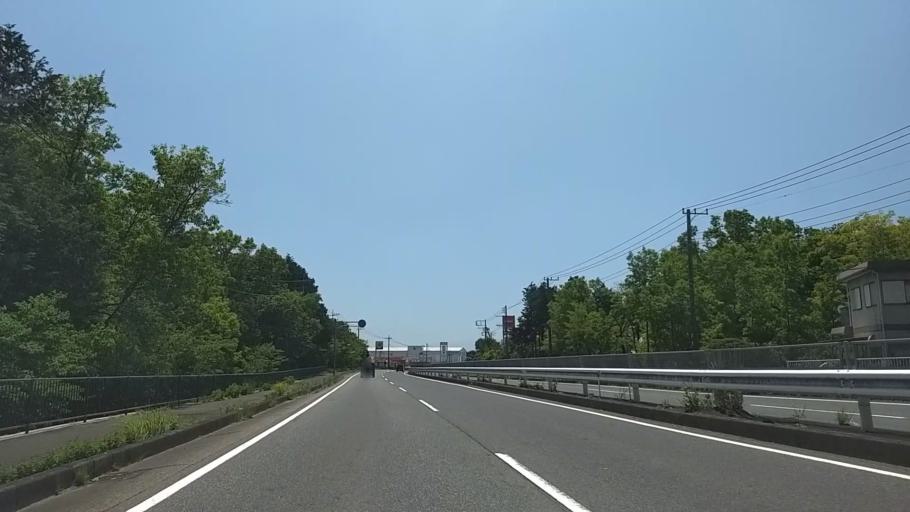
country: JP
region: Shizuoka
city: Gotemba
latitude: 35.2341
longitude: 138.9103
